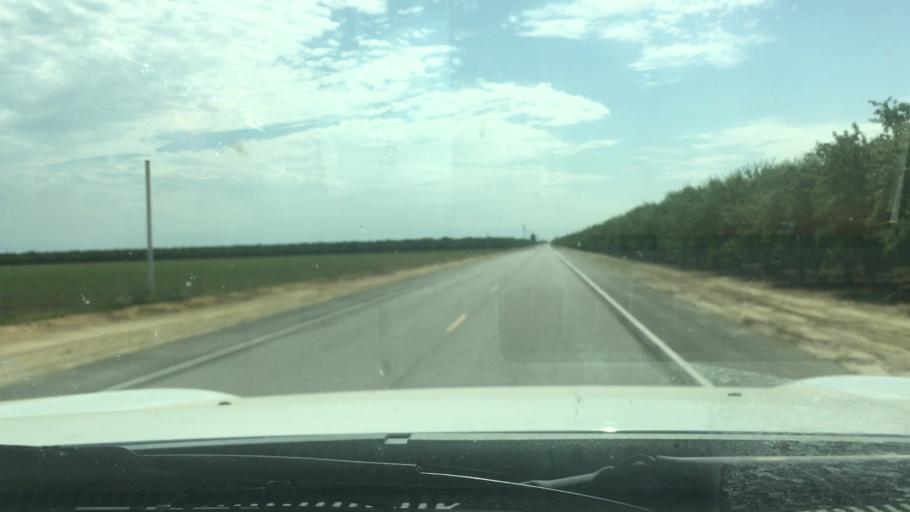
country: US
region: California
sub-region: Kern County
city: Wasco
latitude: 35.5578
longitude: -119.4346
